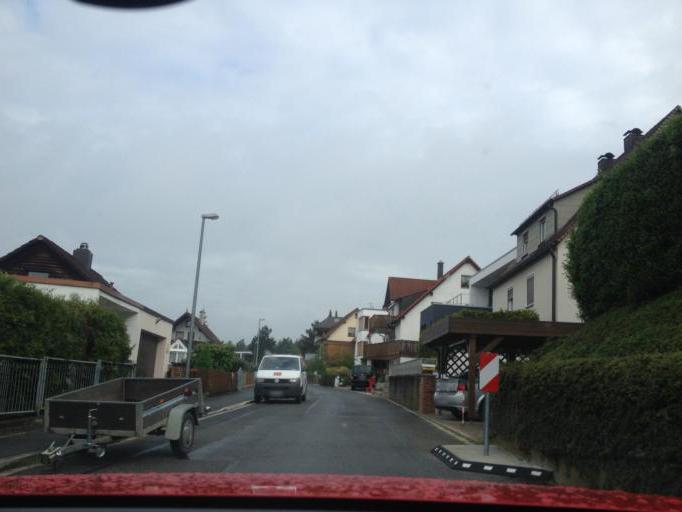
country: DE
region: Bavaria
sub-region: Regierungsbezirk Mittelfranken
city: Lauf an der Pegnitz
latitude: 49.5263
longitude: 11.2709
